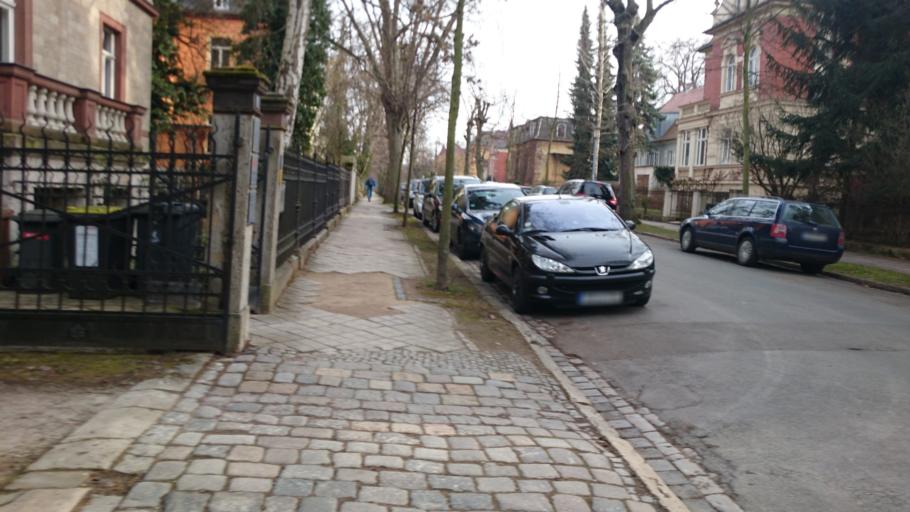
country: DE
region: Thuringia
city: Weimar
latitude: 50.9702
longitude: 11.3301
